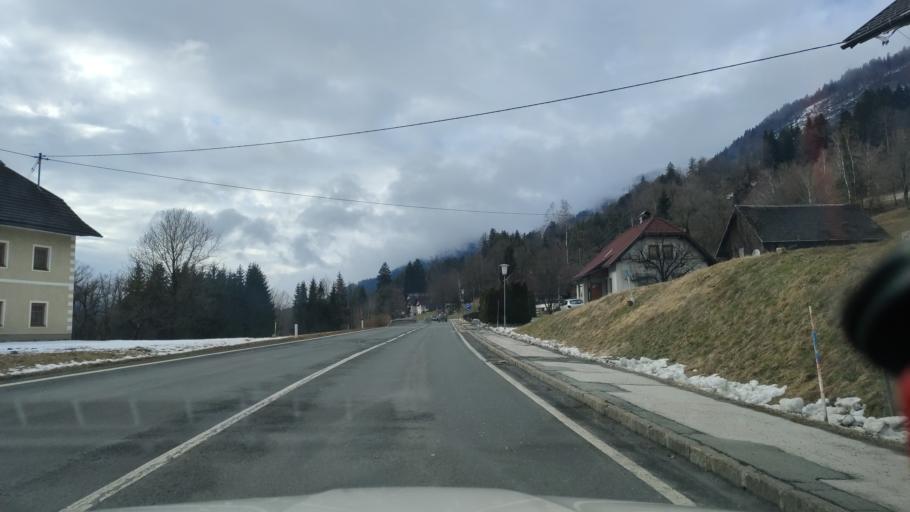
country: AT
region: Carinthia
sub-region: Politischer Bezirk Hermagor
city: Hermagor
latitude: 46.6184
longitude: 13.3335
